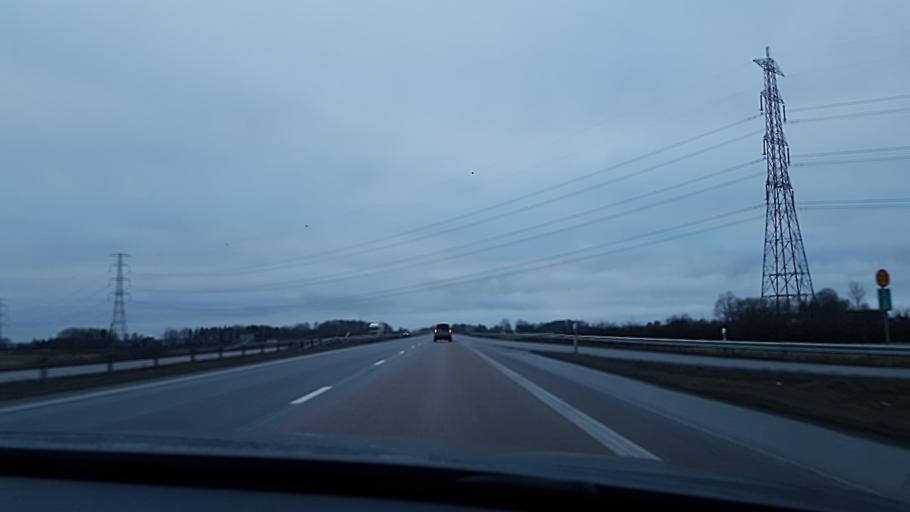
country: SE
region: Skane
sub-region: Astorps Kommun
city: Kvidinge
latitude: 56.1910
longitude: 13.0546
